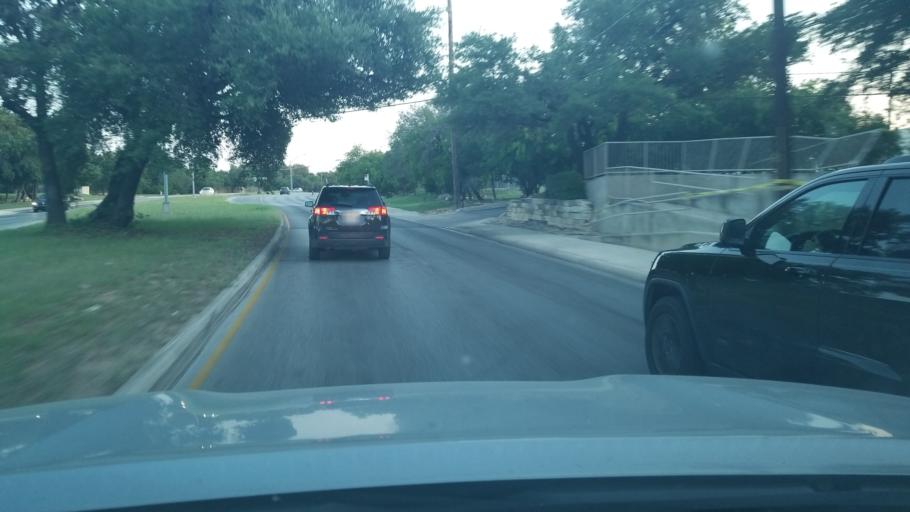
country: US
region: Texas
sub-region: Bexar County
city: Shavano Park
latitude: 29.5805
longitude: -98.5400
